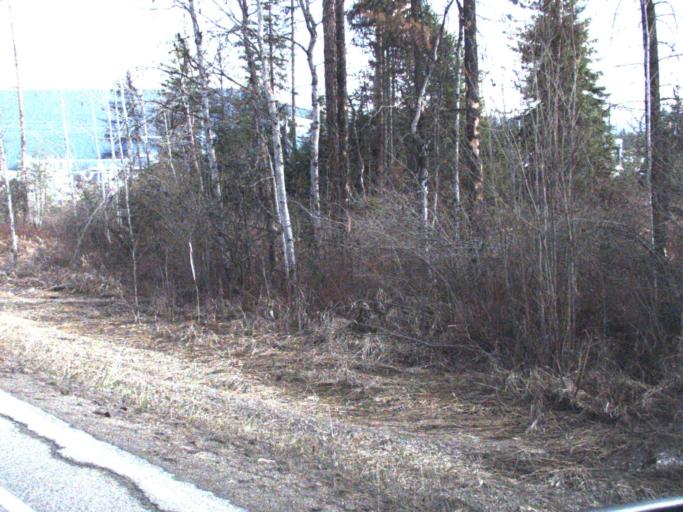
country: US
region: Washington
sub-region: Pend Oreille County
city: Newport
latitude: 48.2869
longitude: -117.2717
